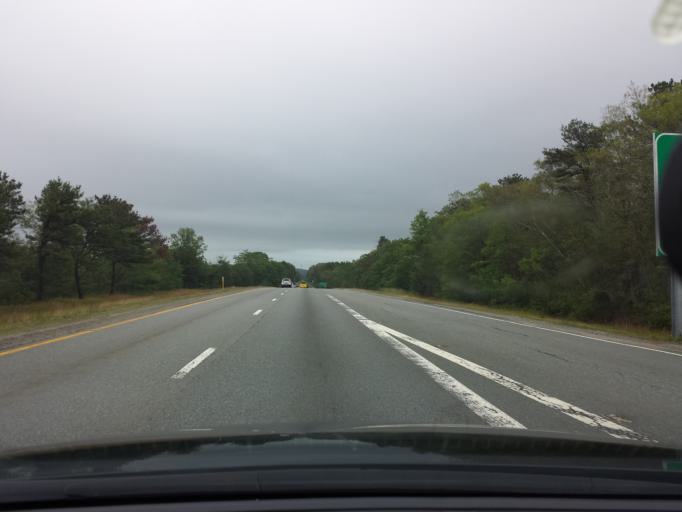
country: US
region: Massachusetts
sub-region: Barnstable County
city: West Barnstable
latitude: 41.7072
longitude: -70.4064
